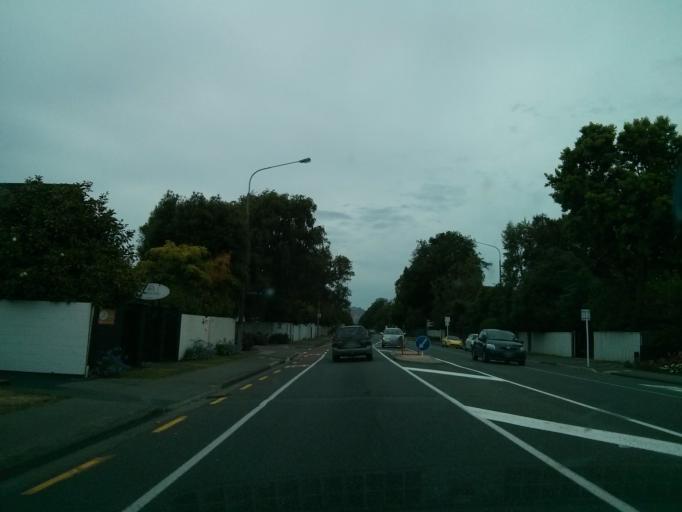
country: NZ
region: Canterbury
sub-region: Christchurch City
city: Christchurch
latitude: -43.5022
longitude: 172.6127
